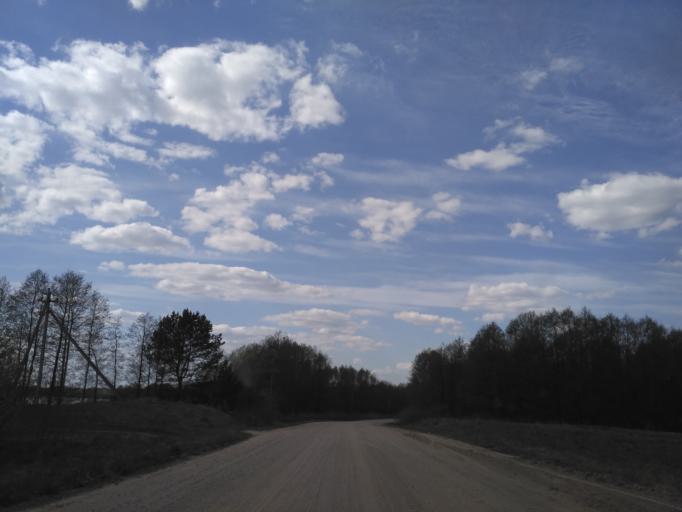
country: BY
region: Minsk
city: Narach
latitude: 54.9951
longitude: 26.5602
